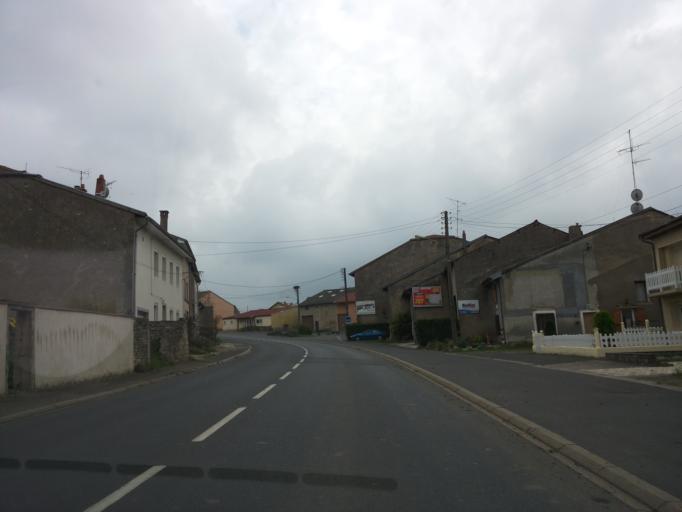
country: FR
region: Lorraine
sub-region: Departement de la Moselle
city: Dieuze
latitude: 48.7214
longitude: 6.7246
